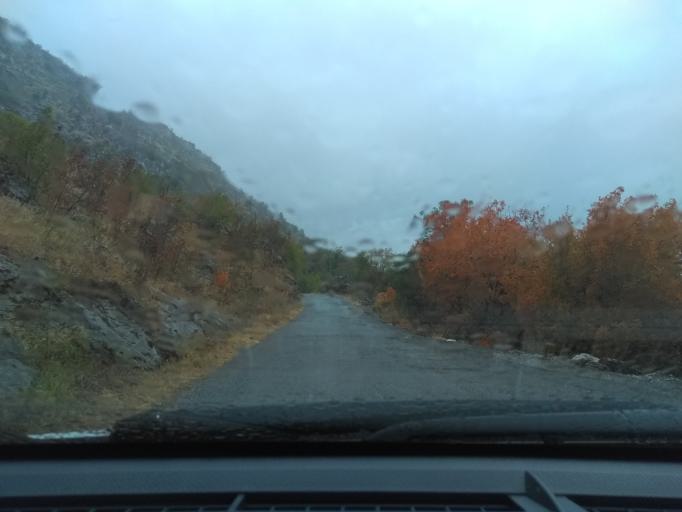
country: ME
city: Stari Bar
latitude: 42.1711
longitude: 19.1899
